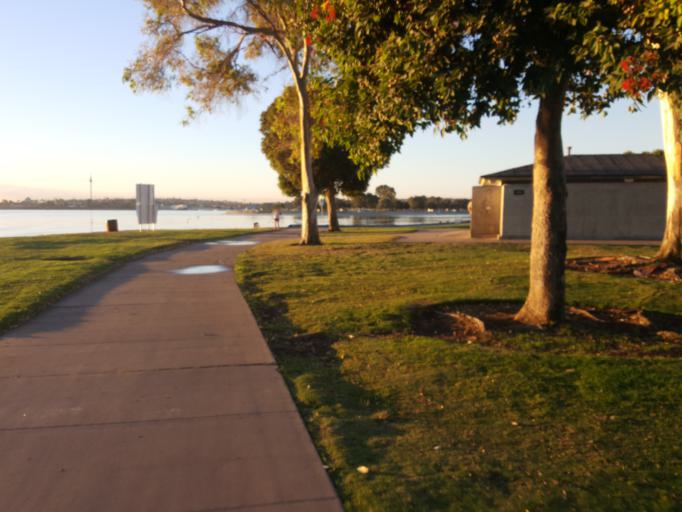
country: US
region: California
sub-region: San Diego County
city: La Jolla
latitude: 32.7832
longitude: -117.2329
